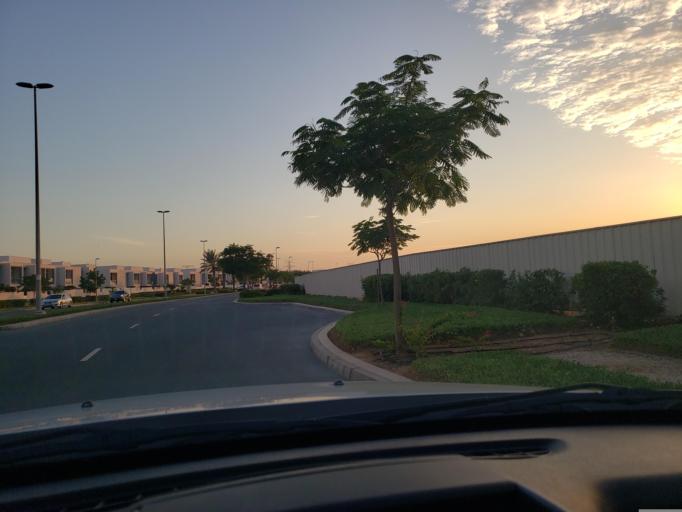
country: AE
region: Dubai
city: Dubai
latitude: 25.0167
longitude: 55.2674
